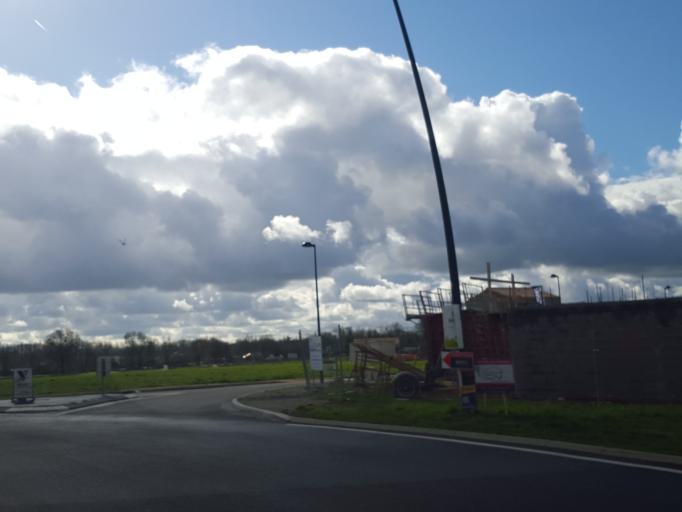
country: FR
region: Pays de la Loire
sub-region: Departement de la Vendee
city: Belleville-sur-Vie
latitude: 46.7748
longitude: -1.4312
